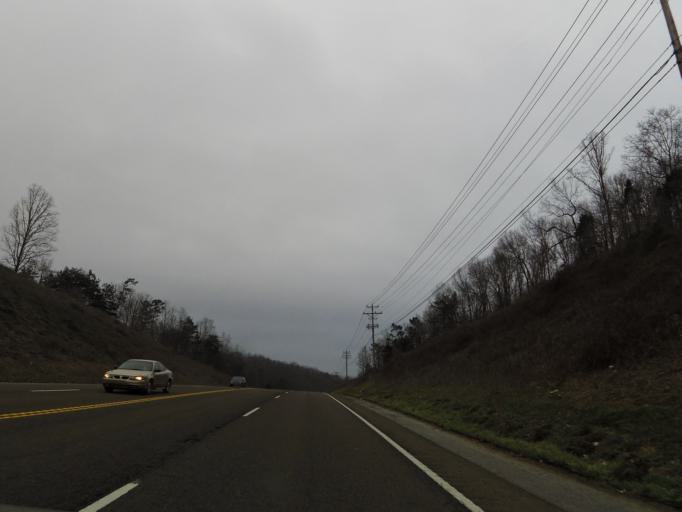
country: US
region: Tennessee
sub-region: Anderson County
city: Clinton
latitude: 36.0539
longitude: -84.1187
